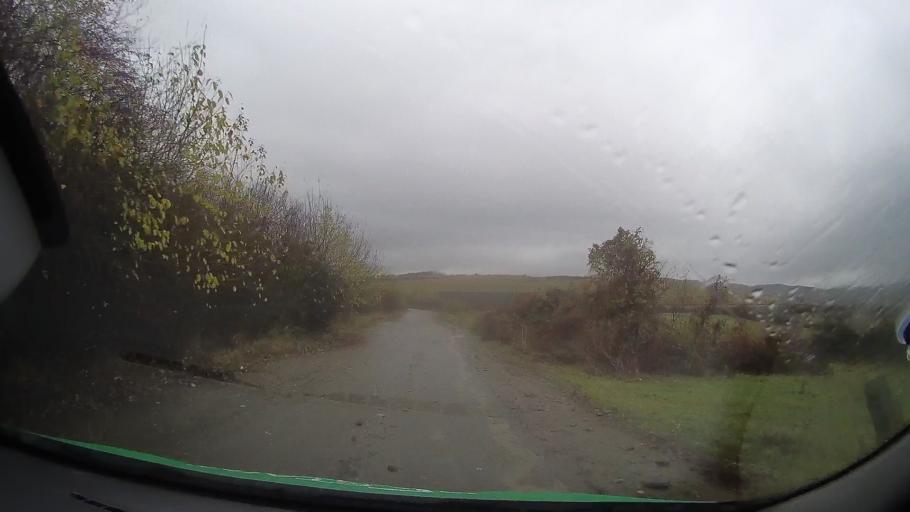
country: RO
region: Mures
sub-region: Comuna Vatava
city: Vatava
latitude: 46.9519
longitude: 24.7345
